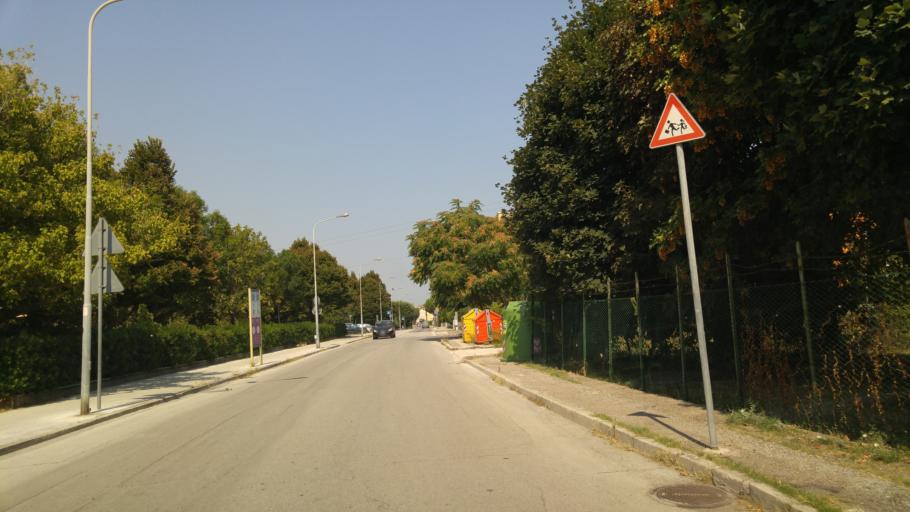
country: IT
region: The Marches
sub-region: Provincia di Pesaro e Urbino
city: Fano
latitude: 43.8350
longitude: 13.0318
